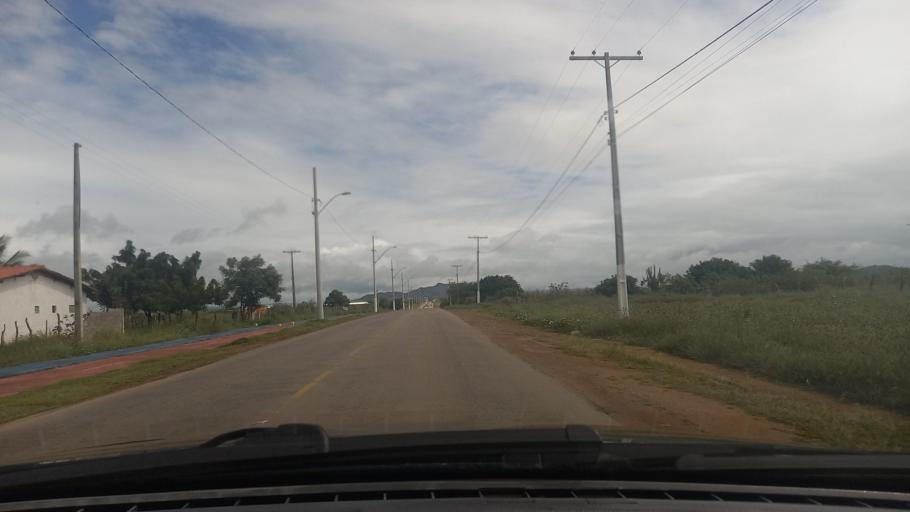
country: BR
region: Bahia
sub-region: Paulo Afonso
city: Paulo Afonso
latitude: -9.3519
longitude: -38.2637
